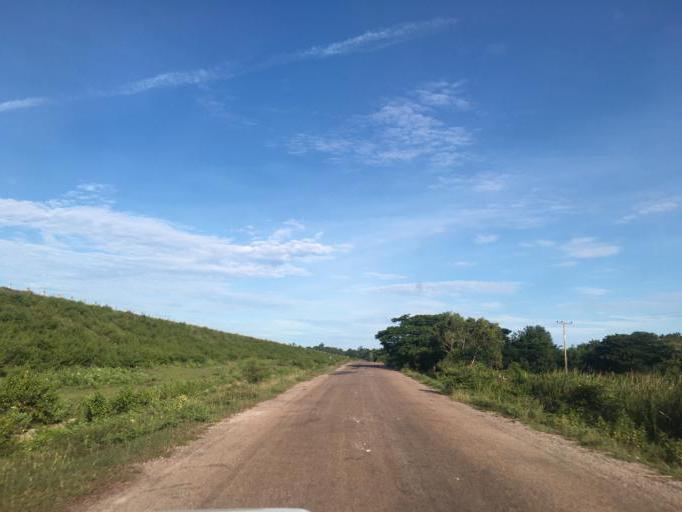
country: TH
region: Changwat Udon Thani
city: Kut Chap
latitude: 17.3597
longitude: 102.5744
